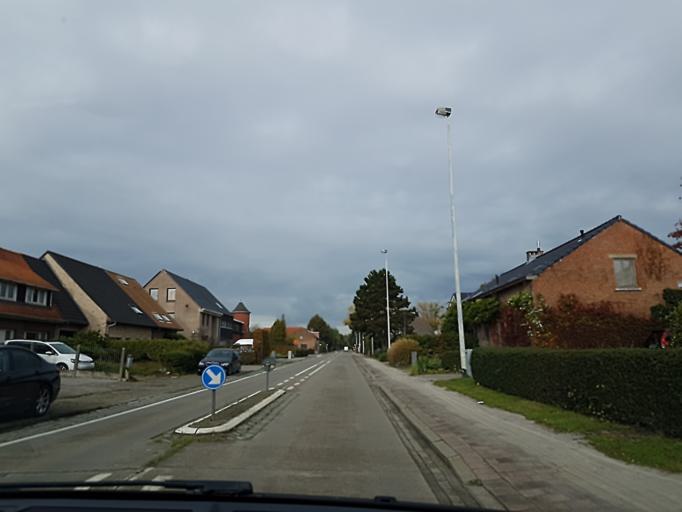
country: BE
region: Flanders
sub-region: Provincie Antwerpen
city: Boechout
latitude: 51.1441
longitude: 4.4873
